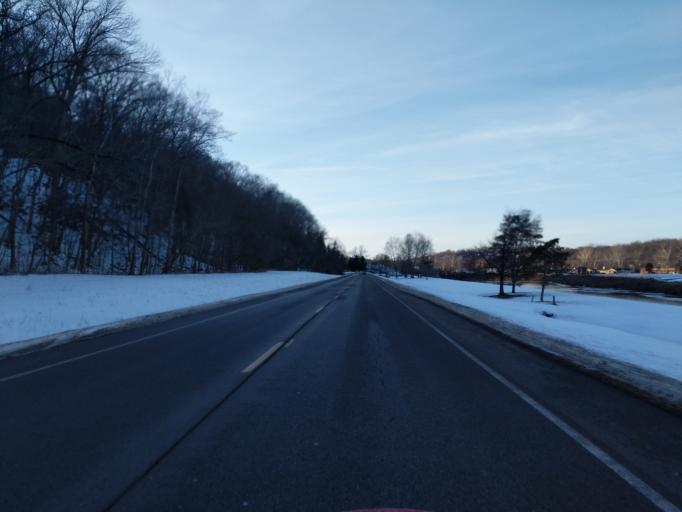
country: US
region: Ohio
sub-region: Athens County
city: Athens
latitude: 39.3271
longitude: -82.1202
